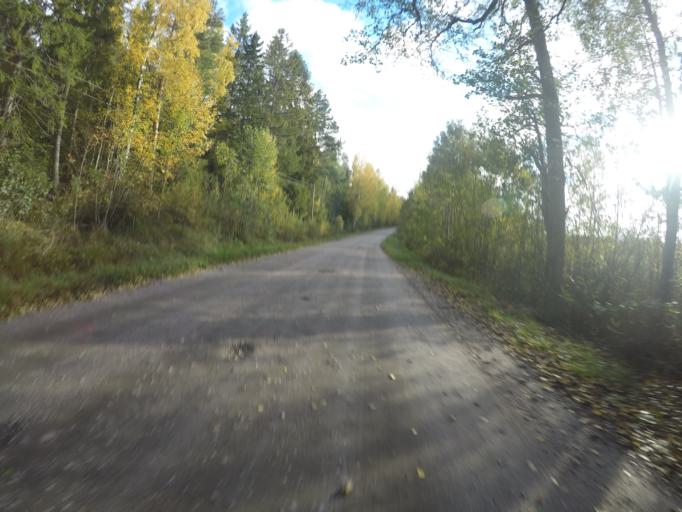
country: SE
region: Vaestmanland
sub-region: Arboga Kommun
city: Tyringe
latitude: 59.3633
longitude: 15.9562
